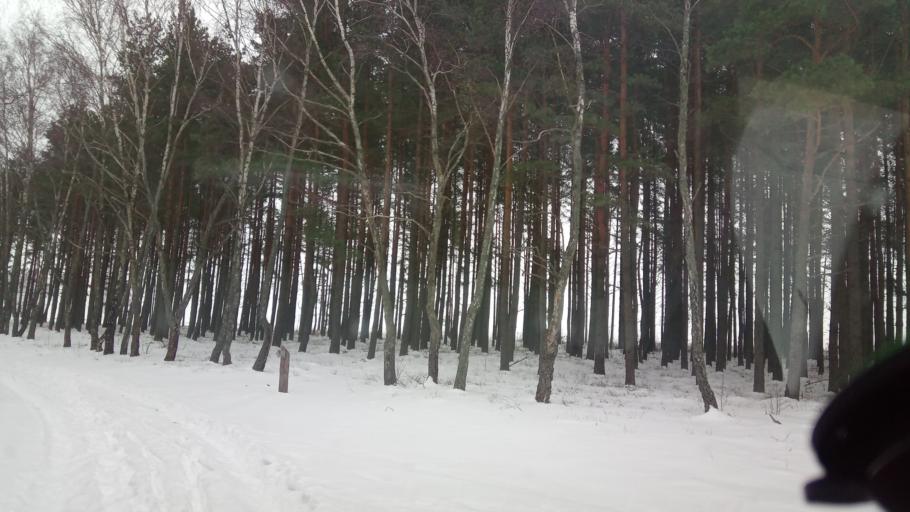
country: LT
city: Neringa
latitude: 55.4211
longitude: 21.1075
